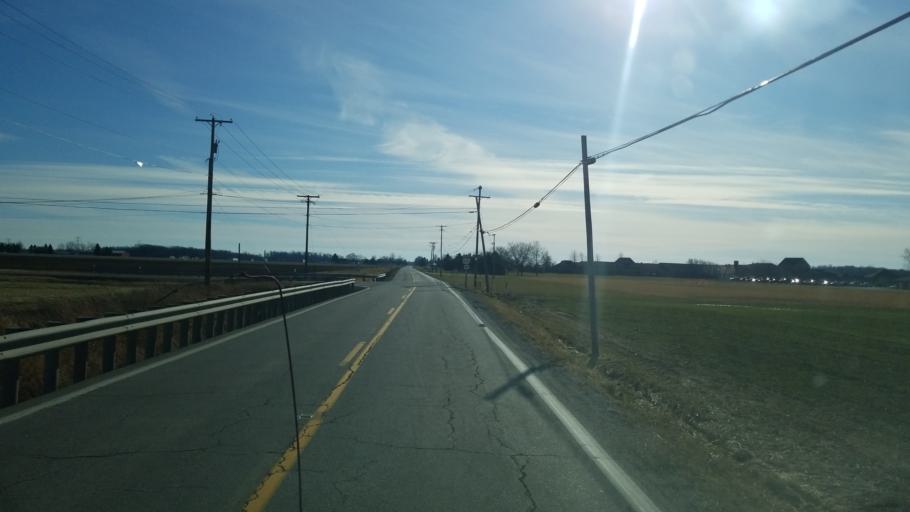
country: US
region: Ohio
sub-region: Wood County
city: Luckey
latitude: 41.4506
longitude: -83.4538
